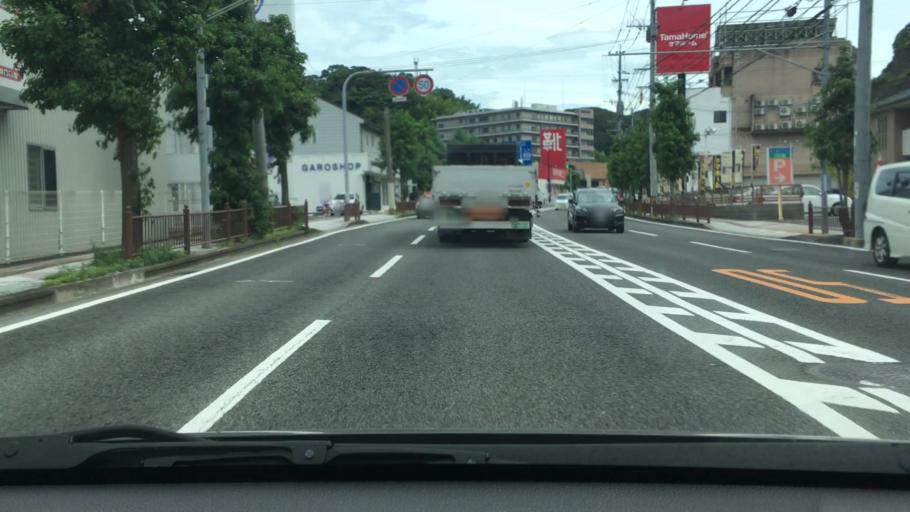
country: JP
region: Nagasaki
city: Togitsu
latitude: 32.8233
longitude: 129.8486
